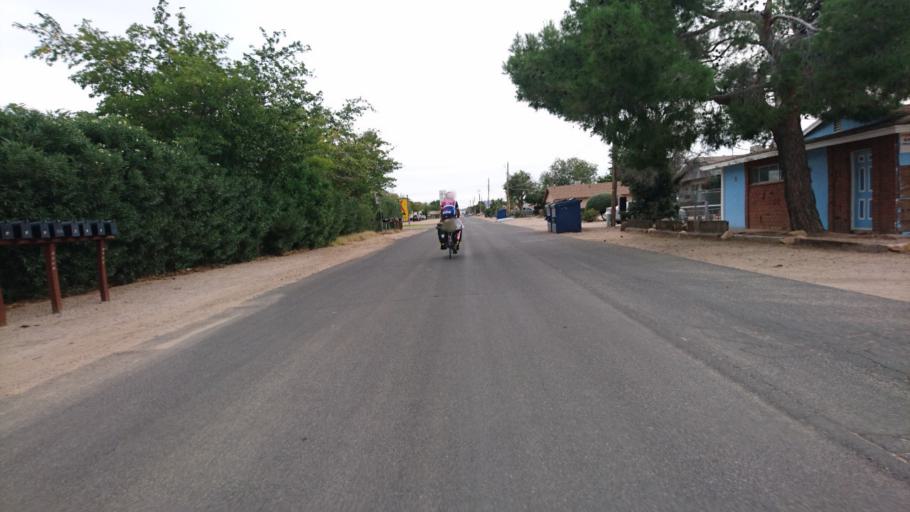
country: US
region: Arizona
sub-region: Mohave County
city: New Kingman-Butler
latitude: 35.2349
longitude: -114.0183
